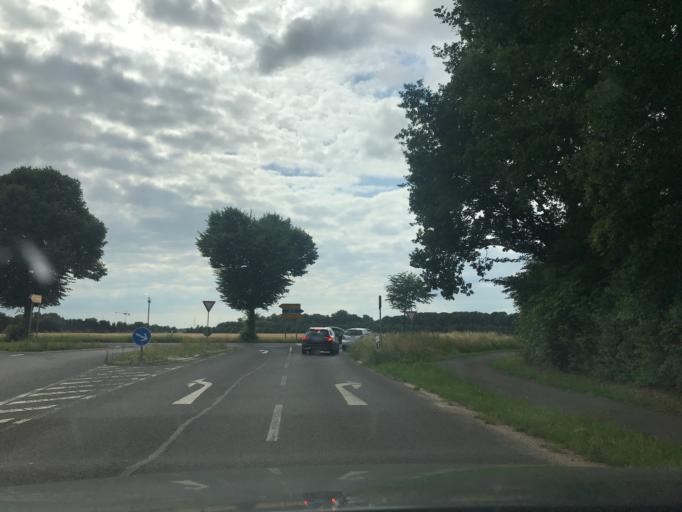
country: DE
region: North Rhine-Westphalia
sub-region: Regierungsbezirk Dusseldorf
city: Neuss
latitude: 51.1496
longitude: 6.7192
